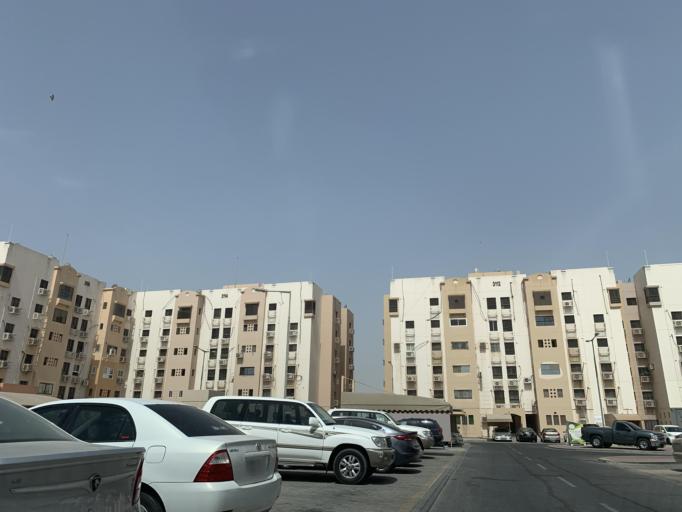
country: BH
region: Northern
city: Madinat `Isa
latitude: 26.1686
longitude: 50.5182
